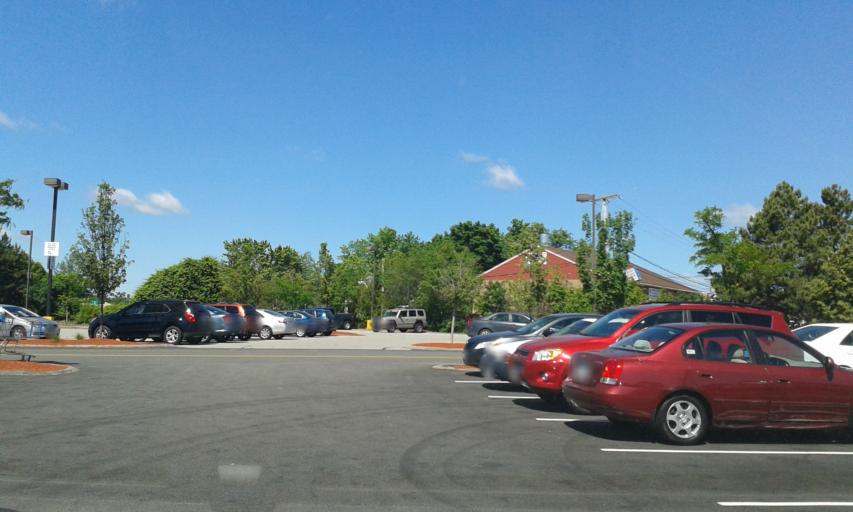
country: US
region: Massachusetts
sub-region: Middlesex County
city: Chelmsford
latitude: 42.6229
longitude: -71.3620
